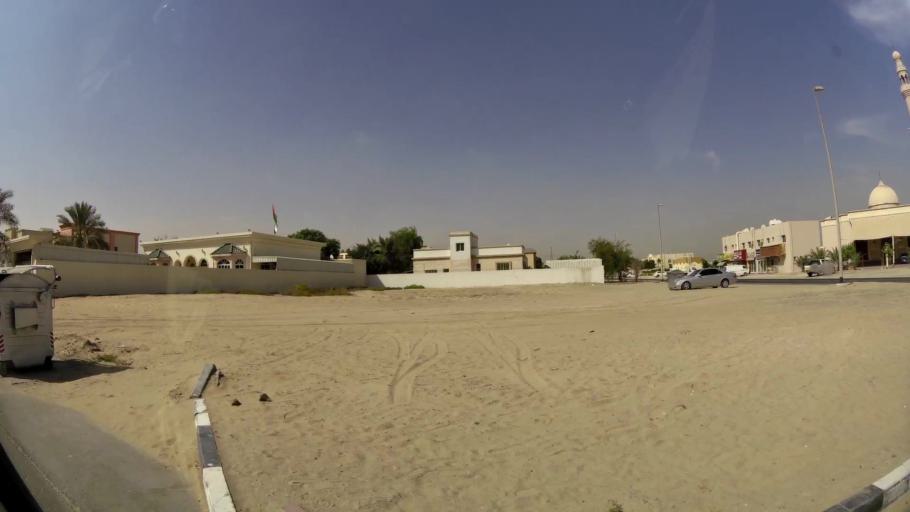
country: AE
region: Ash Shariqah
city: Sharjah
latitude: 25.2698
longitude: 55.4078
